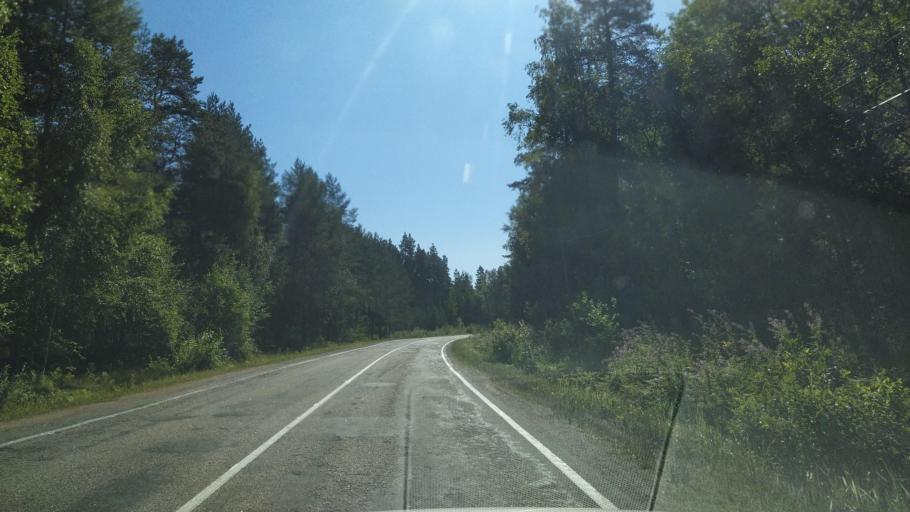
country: RU
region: Leningrad
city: Priozersk
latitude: 60.9887
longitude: 30.2611
